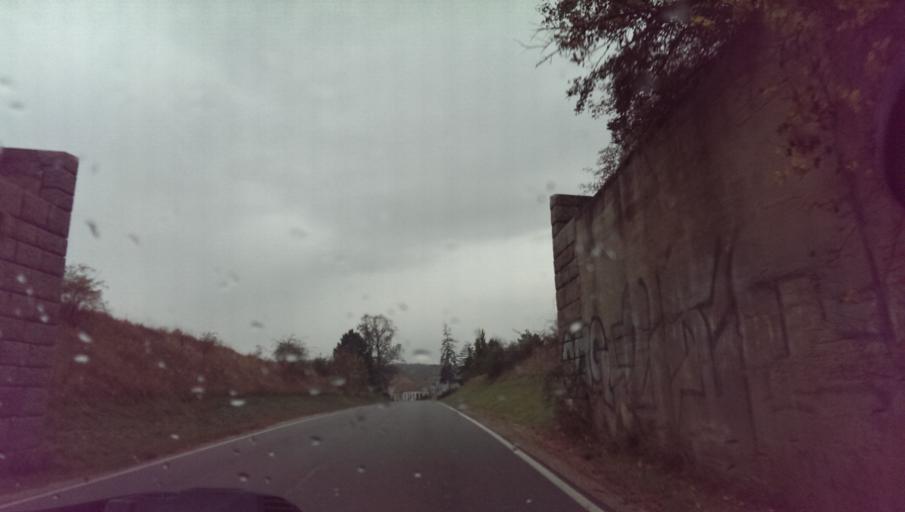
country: CZ
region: South Moravian
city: Ostopovice
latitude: 49.1440
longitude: 16.5573
